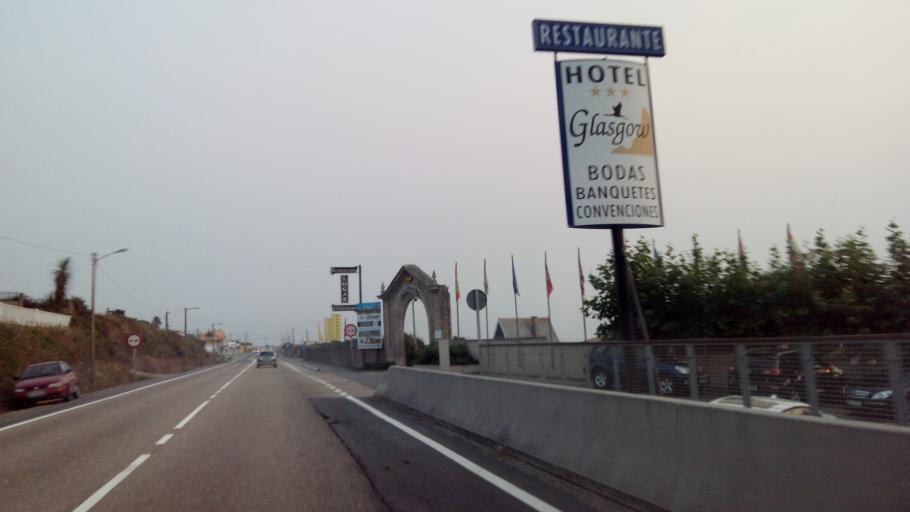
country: ES
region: Galicia
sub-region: Provincia de Pontevedra
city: Oia
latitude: 42.0316
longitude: -8.8827
